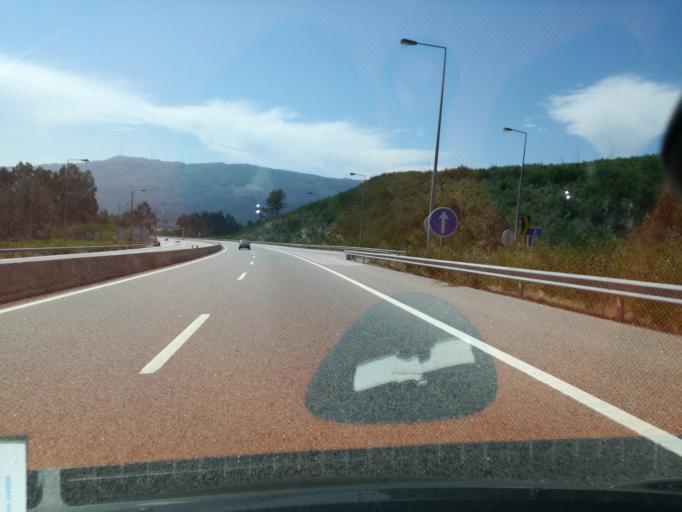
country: PT
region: Viana do Castelo
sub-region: Caminha
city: Vila Praia de Ancora
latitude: 41.8149
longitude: -8.8050
